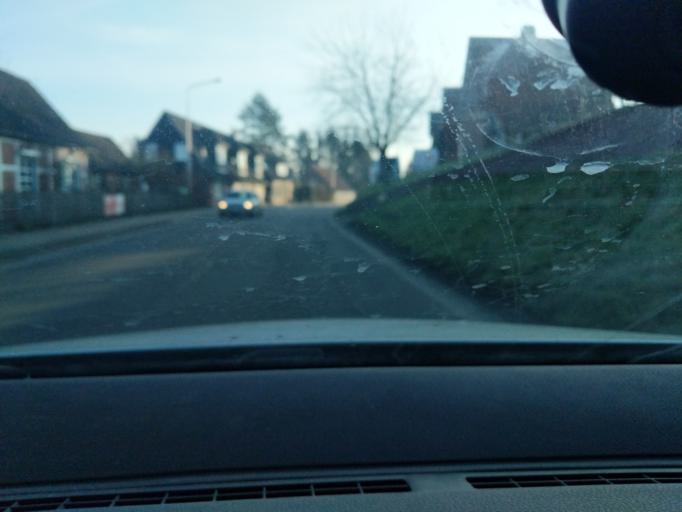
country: DE
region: Lower Saxony
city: Mittelnkirchen
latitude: 53.5428
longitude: 9.6201
